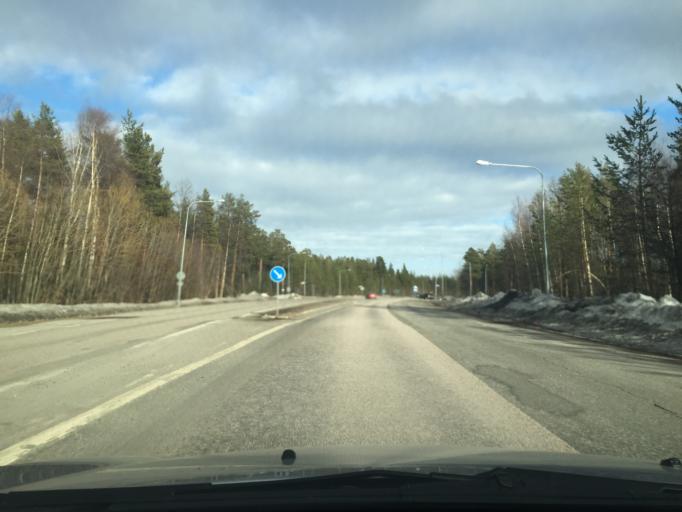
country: SE
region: Norrbotten
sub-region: Lulea Kommun
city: Lulea
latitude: 65.5926
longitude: 22.2406
